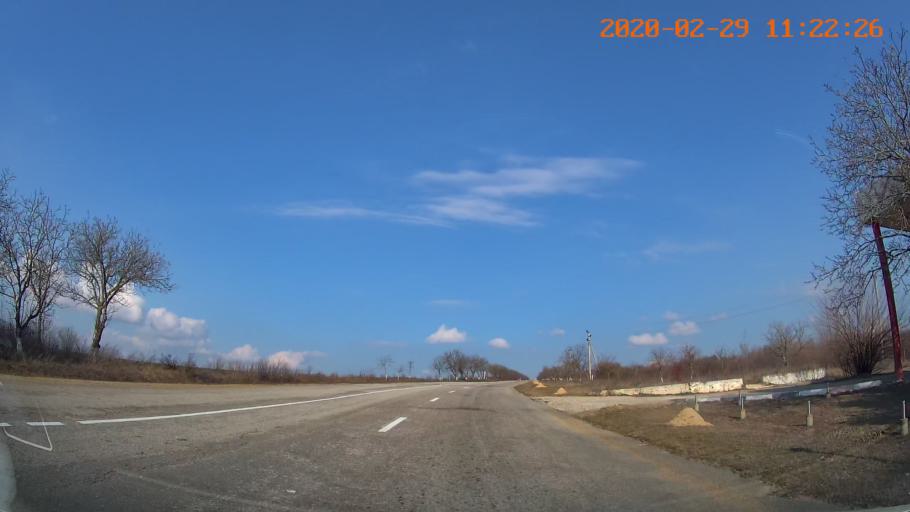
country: MD
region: Telenesti
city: Cocieri
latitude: 47.3939
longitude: 29.1619
